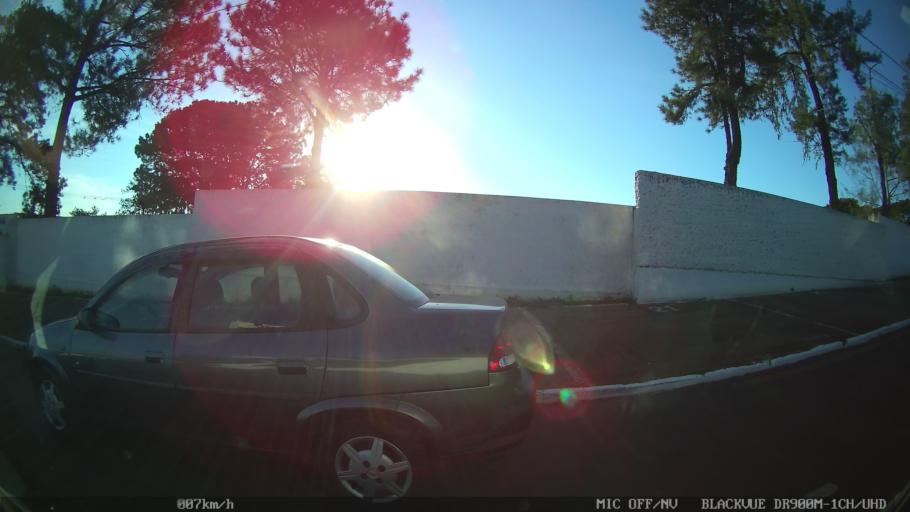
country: BR
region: Sao Paulo
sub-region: Franca
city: Franca
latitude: -20.5180
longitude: -47.3820
